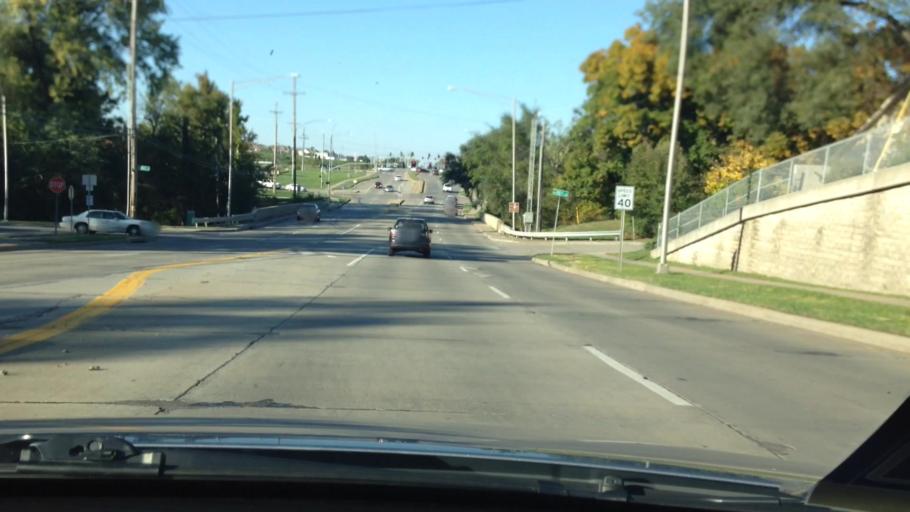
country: US
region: Missouri
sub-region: Clay County
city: Gladstone
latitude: 39.2569
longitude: -94.5758
